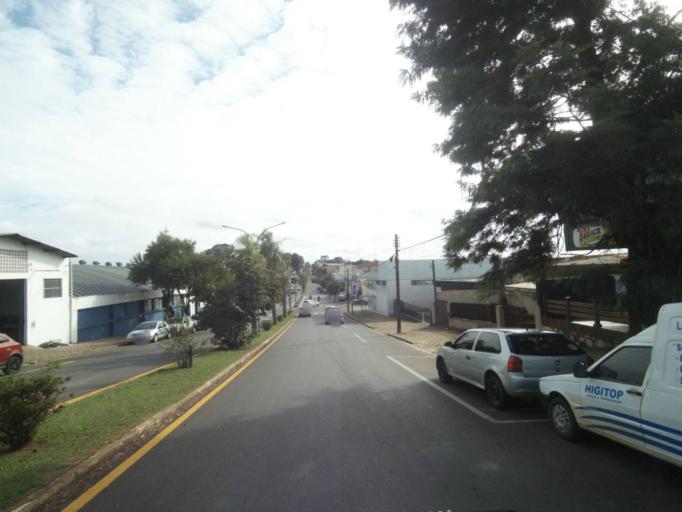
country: BR
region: Parana
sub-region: Telemaco Borba
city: Telemaco Borba
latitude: -24.3345
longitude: -50.6260
